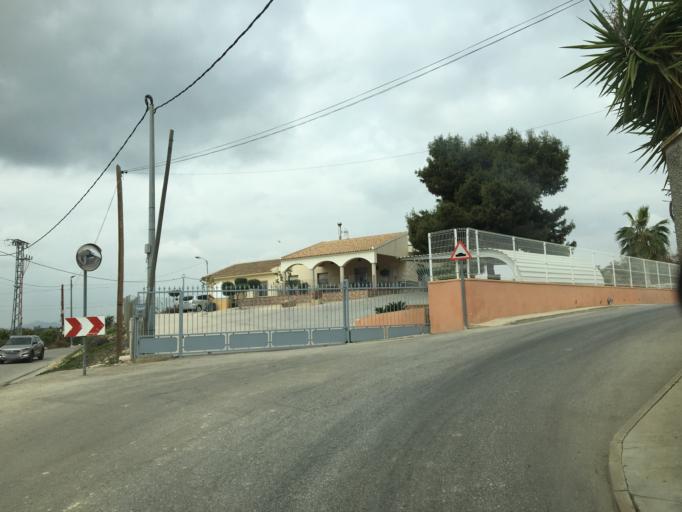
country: ES
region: Murcia
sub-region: Murcia
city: Beniel
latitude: 38.0289
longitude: -0.9807
